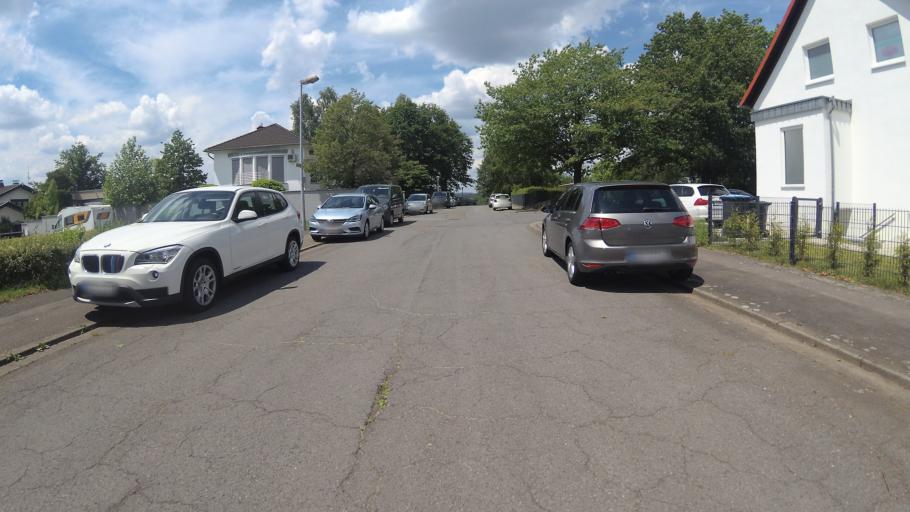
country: DE
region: Saarland
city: Homburg
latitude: 49.3124
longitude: 7.3153
